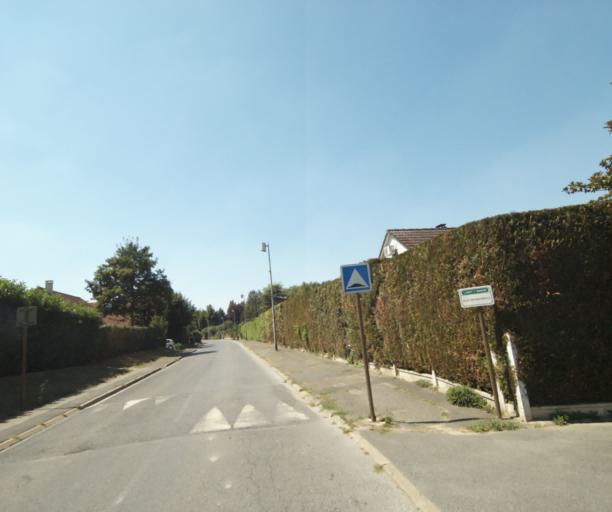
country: FR
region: Ile-de-France
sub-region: Departement de Seine-et-Marne
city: Thorigny-sur-Marne
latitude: 48.8817
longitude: 2.7259
